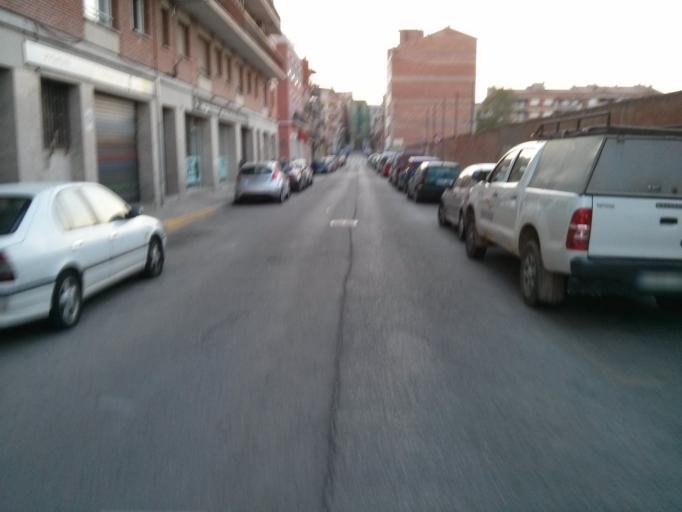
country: ES
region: Catalonia
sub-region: Provincia de Barcelona
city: Manresa
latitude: 41.7232
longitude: 1.8186
